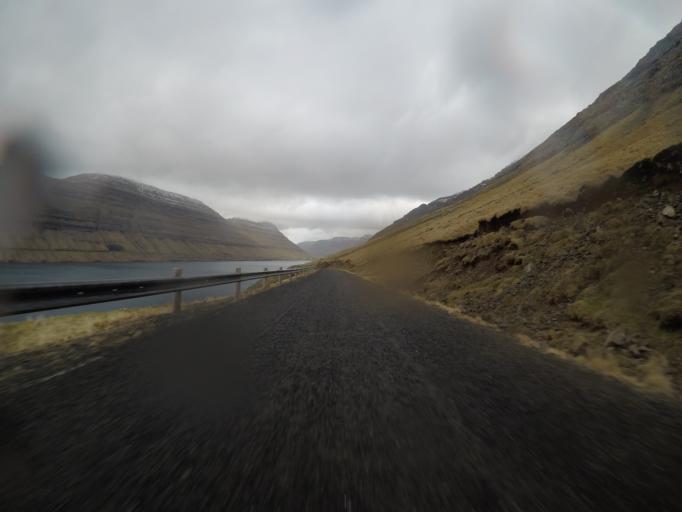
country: FO
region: Nordoyar
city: Klaksvik
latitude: 62.3270
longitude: -6.5670
